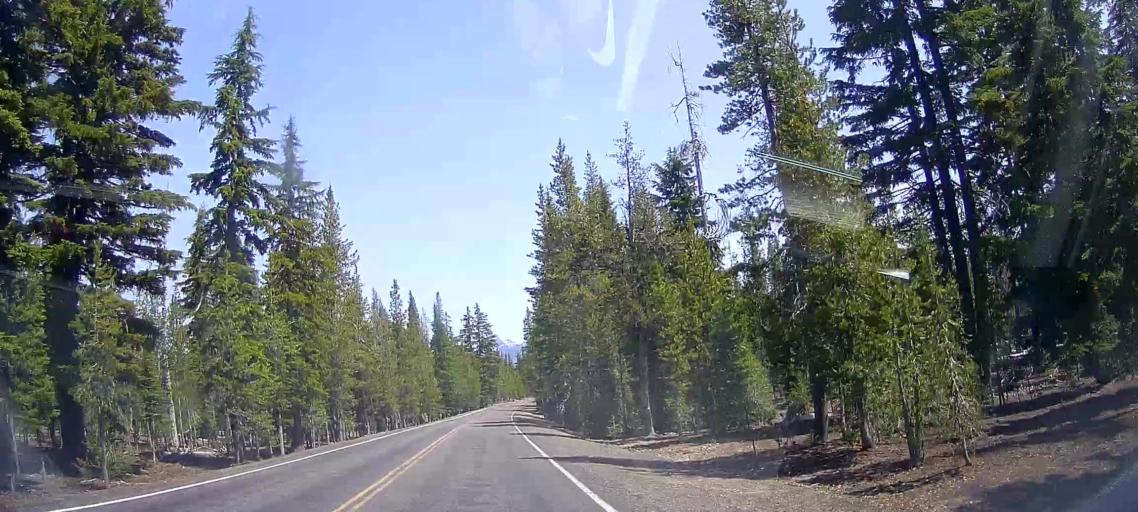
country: US
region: Oregon
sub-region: Jackson County
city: Shady Cove
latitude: 43.0056
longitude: -122.1333
